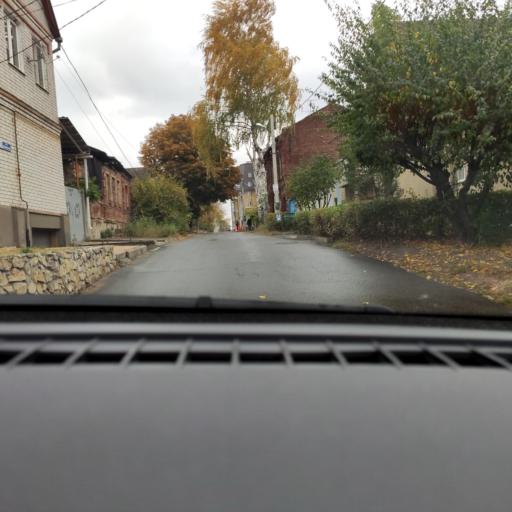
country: RU
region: Voronezj
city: Voronezh
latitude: 51.6822
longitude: 39.2189
